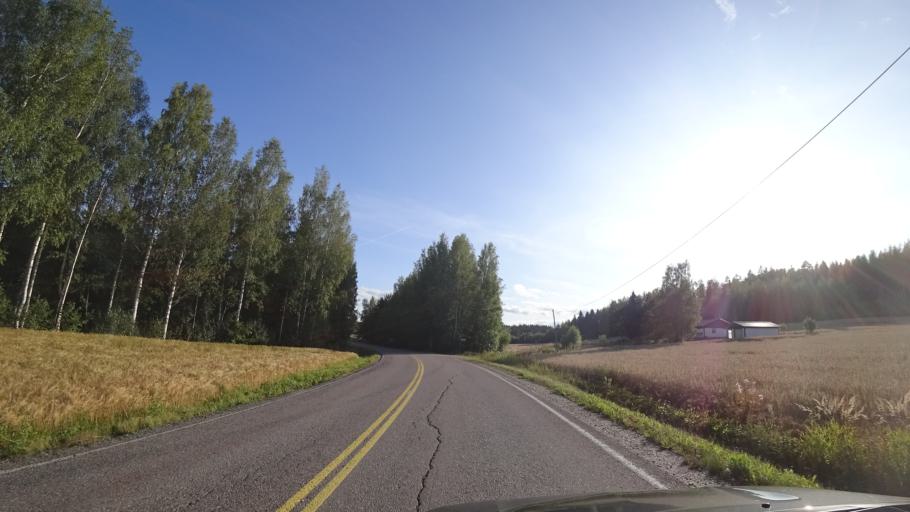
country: FI
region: Paijanne Tavastia
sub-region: Lahti
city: Asikkala
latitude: 61.1788
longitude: 25.3770
